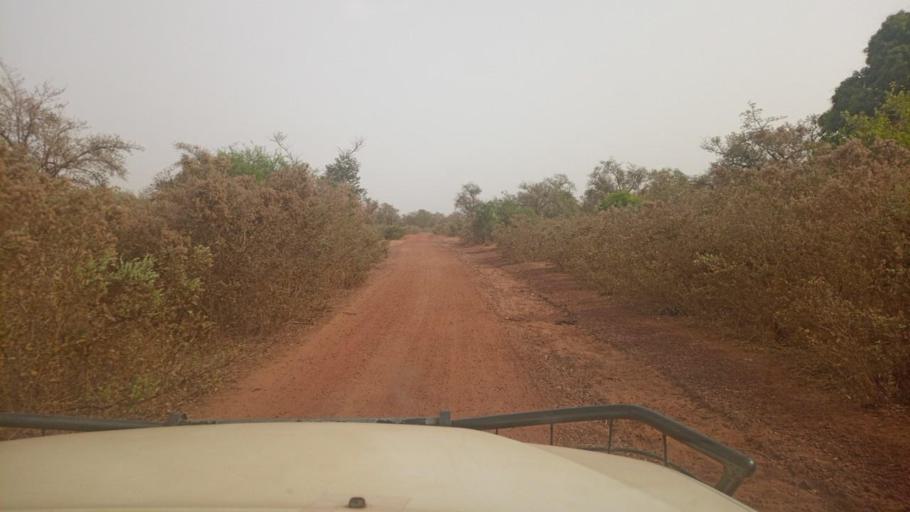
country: BF
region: Boucle du Mouhoun
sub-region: Province des Banwa
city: Salanso
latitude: 12.1089
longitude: -4.3362
